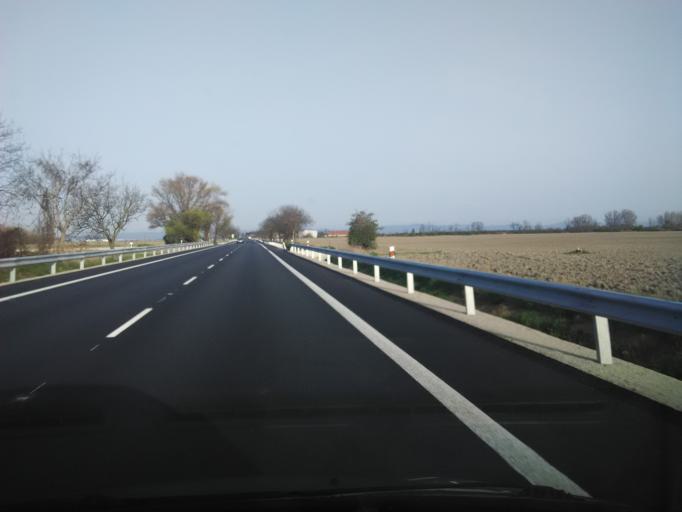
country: SK
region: Trnavsky
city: Sladkovicovo
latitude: 48.1998
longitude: 17.5630
